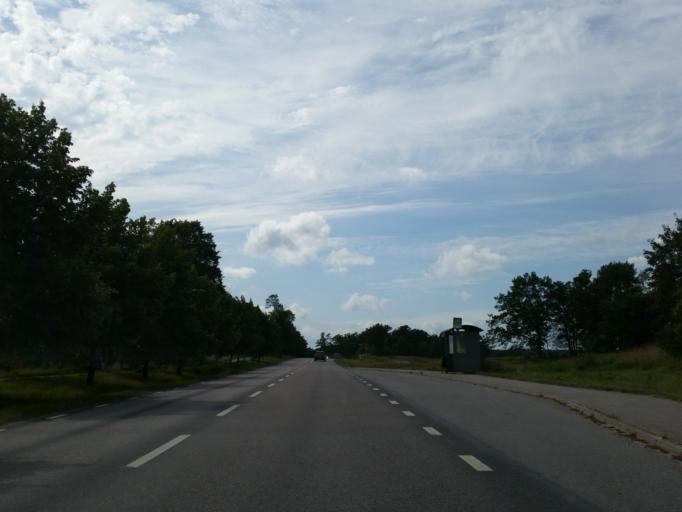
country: SE
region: Soedermanland
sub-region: Strangnas Kommun
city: Mariefred
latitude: 59.2582
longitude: 17.2113
